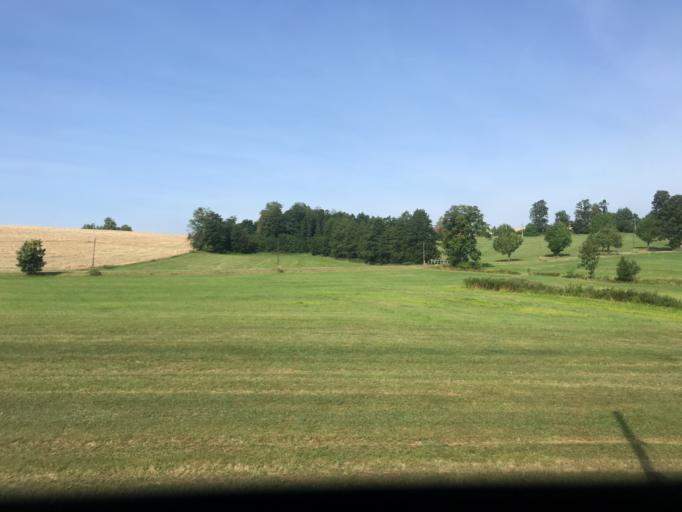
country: CZ
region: Jihocesky
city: Chotoviny
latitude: 49.5469
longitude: 14.6151
